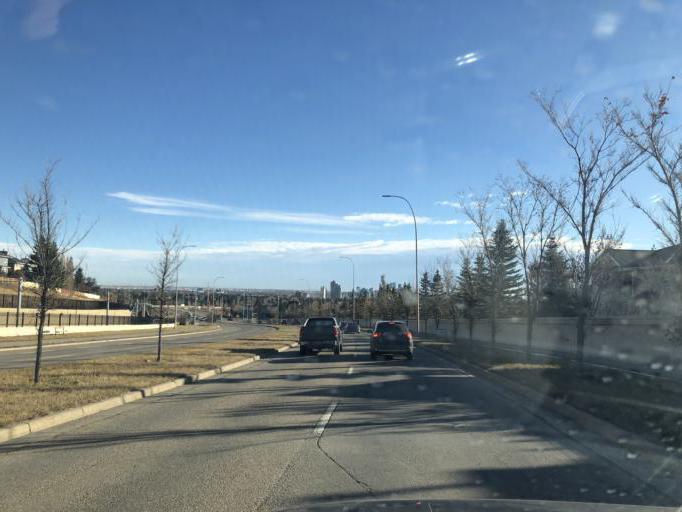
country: CA
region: Alberta
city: Calgary
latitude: 51.0364
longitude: -114.1743
